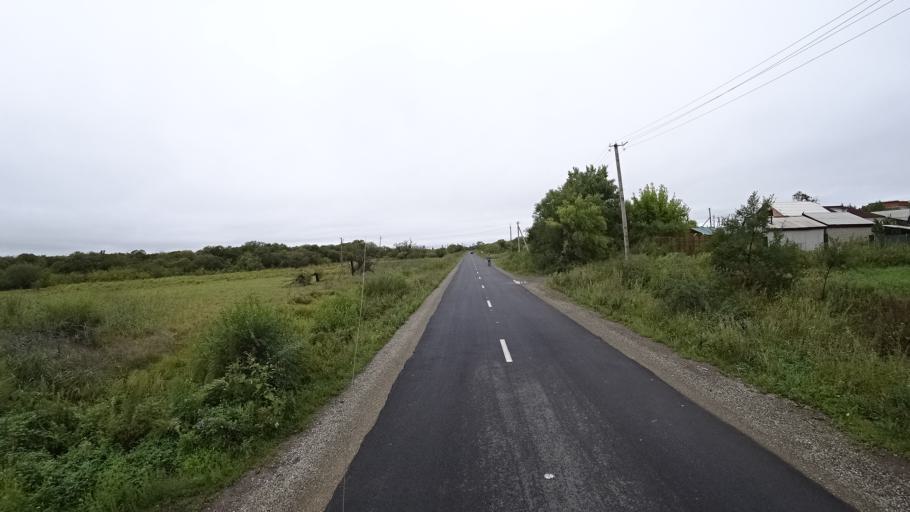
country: RU
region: Primorskiy
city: Monastyrishche
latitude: 44.1997
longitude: 132.4467
